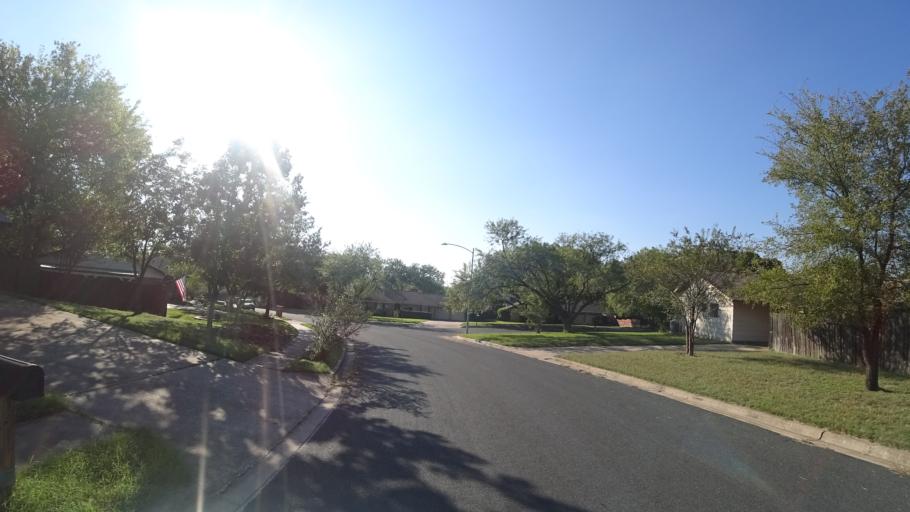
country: US
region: Texas
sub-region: Travis County
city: Wells Branch
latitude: 30.3550
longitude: -97.6745
